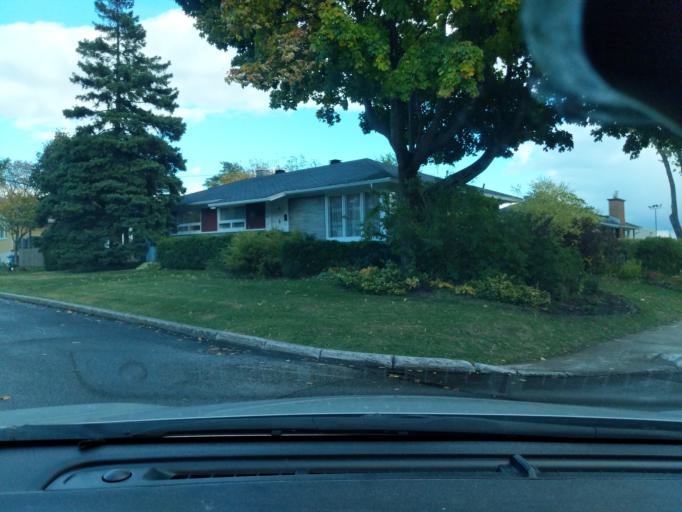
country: CA
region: Quebec
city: L'Ancienne-Lorette
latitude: 46.7628
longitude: -71.2851
